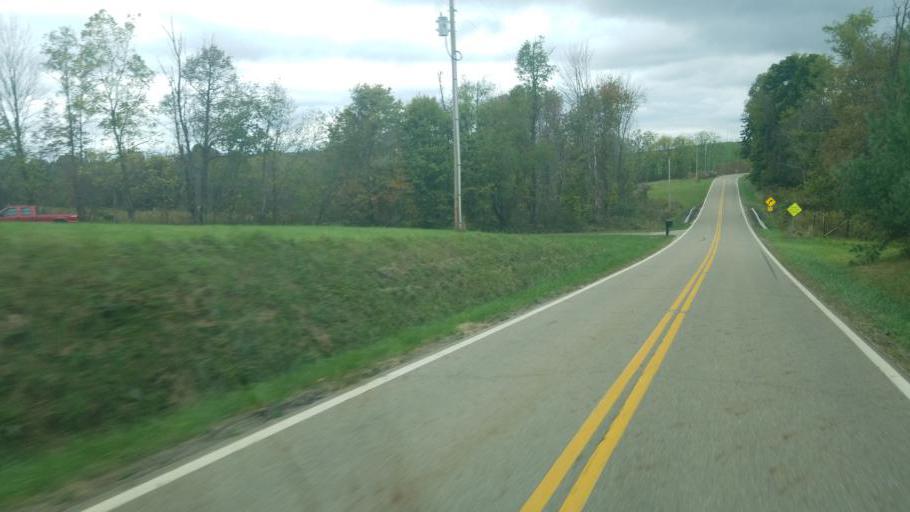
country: US
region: Ohio
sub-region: Knox County
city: Danville
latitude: 40.5255
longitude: -82.1534
